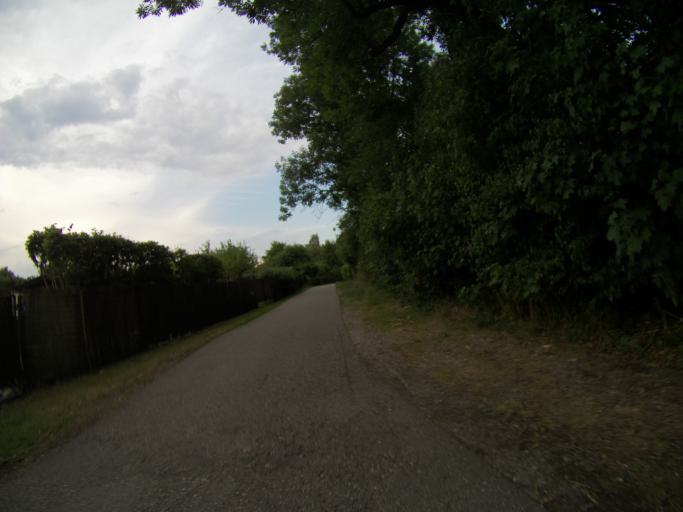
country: DE
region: Bavaria
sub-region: Upper Bavaria
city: Freising
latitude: 48.3928
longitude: 11.7446
